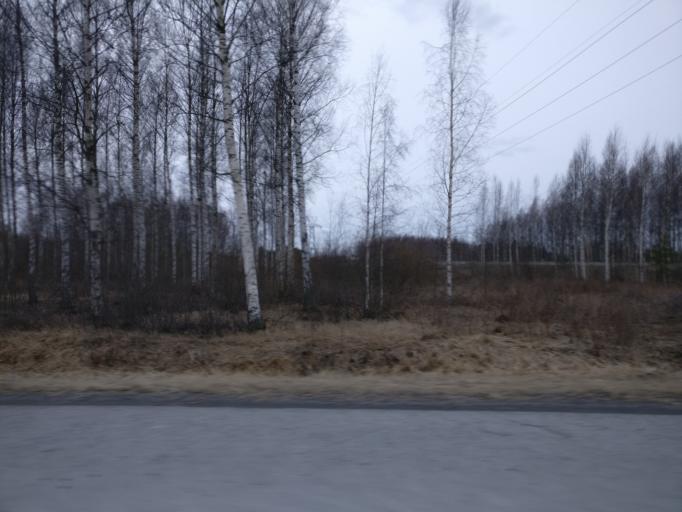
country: FI
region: Pirkanmaa
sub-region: Etelae-Pirkanmaa
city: Toijala
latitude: 61.2048
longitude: 23.8403
